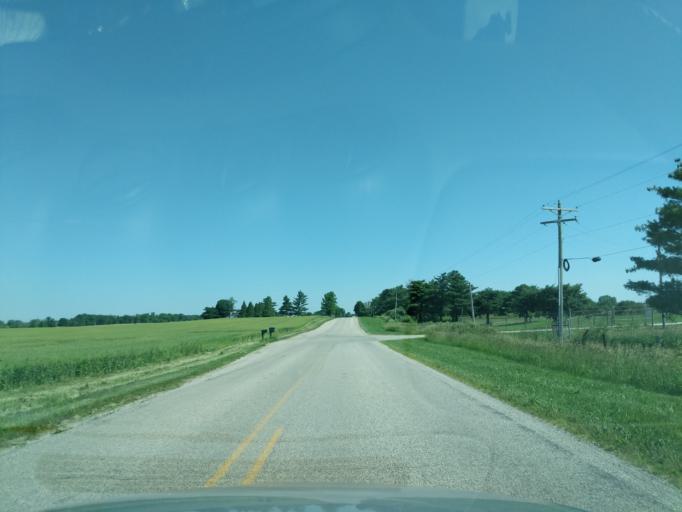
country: US
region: Indiana
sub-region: Huntington County
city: Huntington
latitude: 40.8209
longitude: -85.5083
